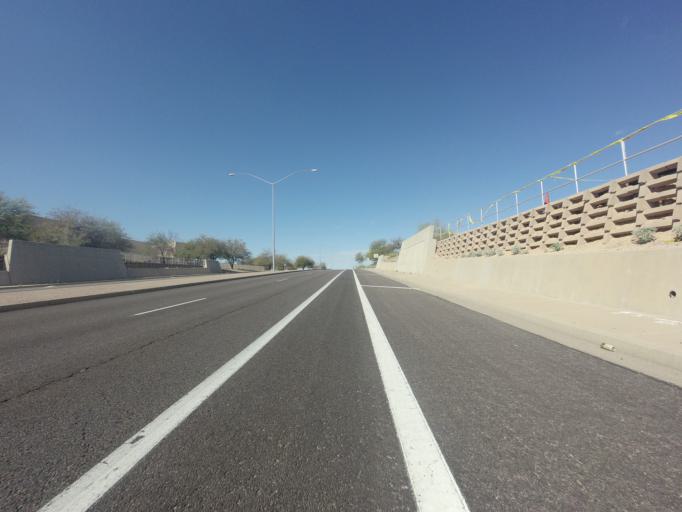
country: US
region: Arizona
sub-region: Maricopa County
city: Mesa
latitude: 33.4665
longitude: -111.7289
